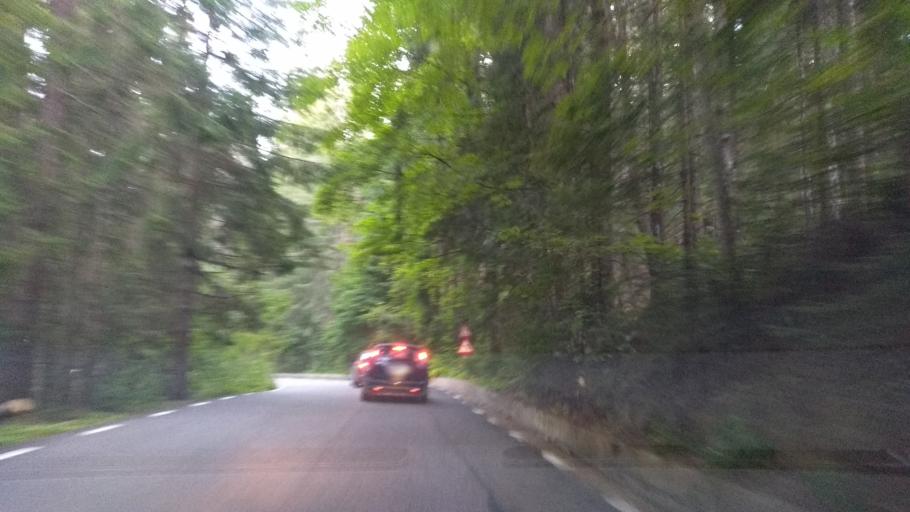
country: RO
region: Prahova
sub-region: Oras Sinaia
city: Sinaia
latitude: 45.3218
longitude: 25.5141
